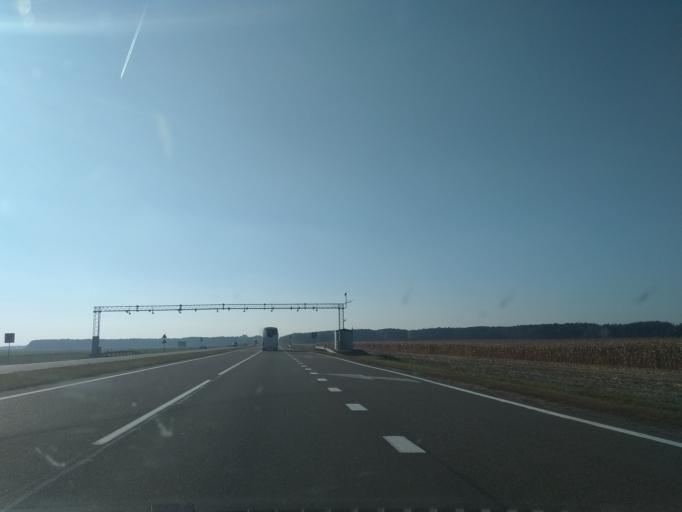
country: BY
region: Brest
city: Zhabinka
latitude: 52.1418
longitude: 23.9803
